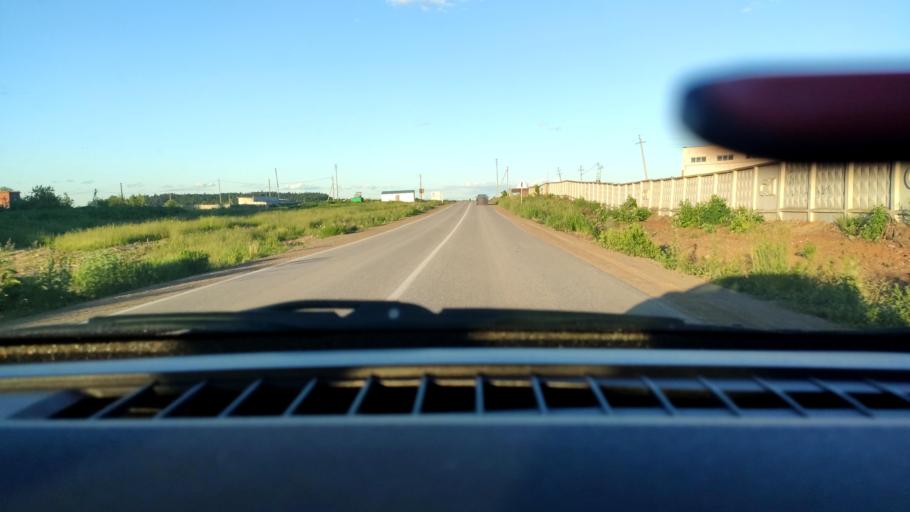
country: RU
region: Perm
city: Kultayevo
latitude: 57.9241
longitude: 55.9056
